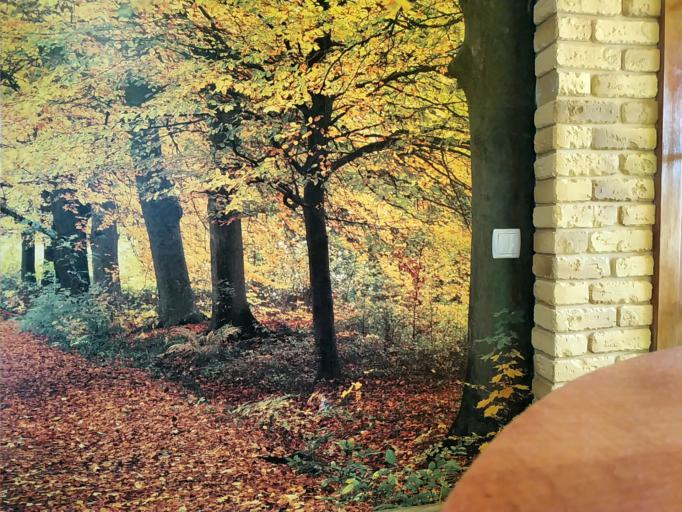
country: RU
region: Pskov
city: Dno
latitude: 57.9103
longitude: 30.1823
